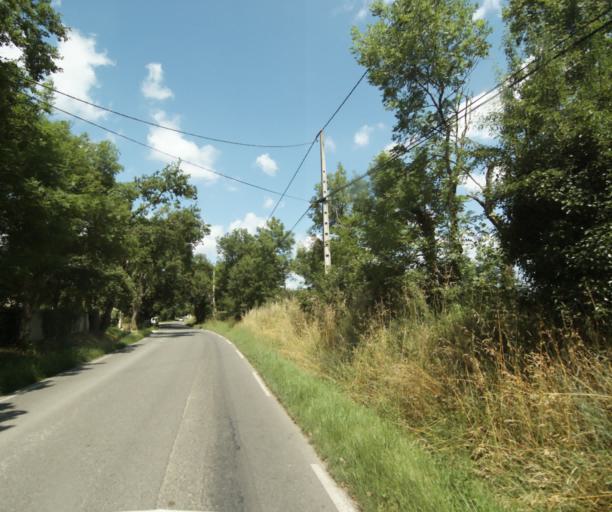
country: FR
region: Midi-Pyrenees
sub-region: Departement du Tarn-et-Garonne
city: Montauban
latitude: 44.0380
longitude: 1.3501
